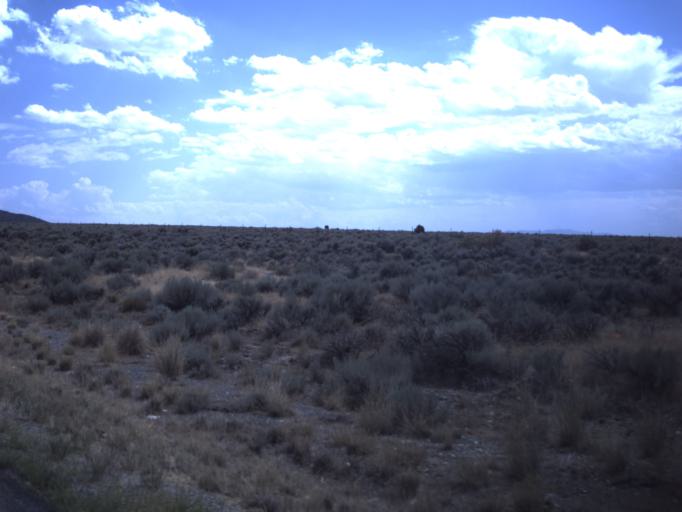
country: US
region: Utah
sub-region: Tooele County
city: Tooele
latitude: 40.3582
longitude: -112.3213
